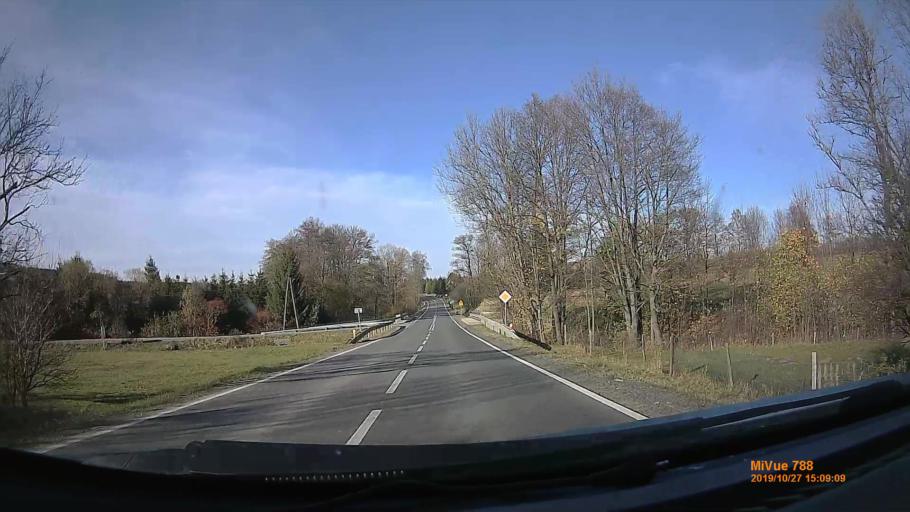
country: PL
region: Lower Silesian Voivodeship
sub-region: Powiat klodzki
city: Miedzylesie
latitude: 50.1772
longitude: 16.6696
